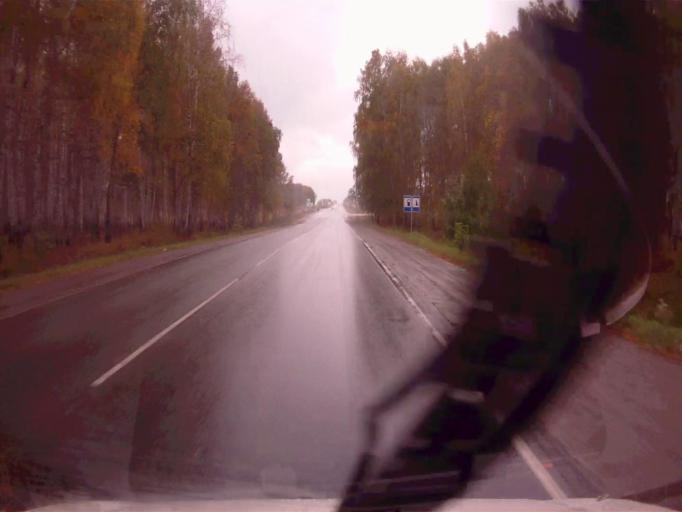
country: RU
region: Chelyabinsk
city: Argayash
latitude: 55.4151
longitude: 61.0312
